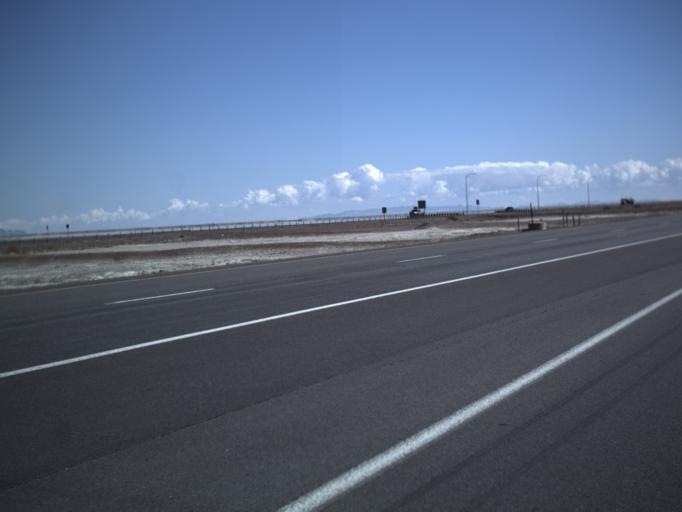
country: US
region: Utah
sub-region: Tooele County
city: Wendover
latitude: 40.7384
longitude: -113.8540
